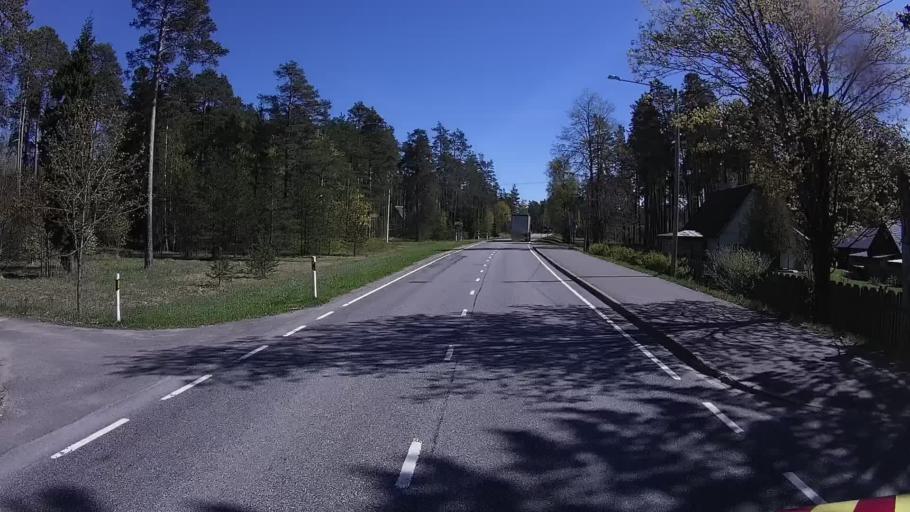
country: EE
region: Harju
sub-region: Kuusalu vald
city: Kuusalu
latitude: 59.2815
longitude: 25.6145
